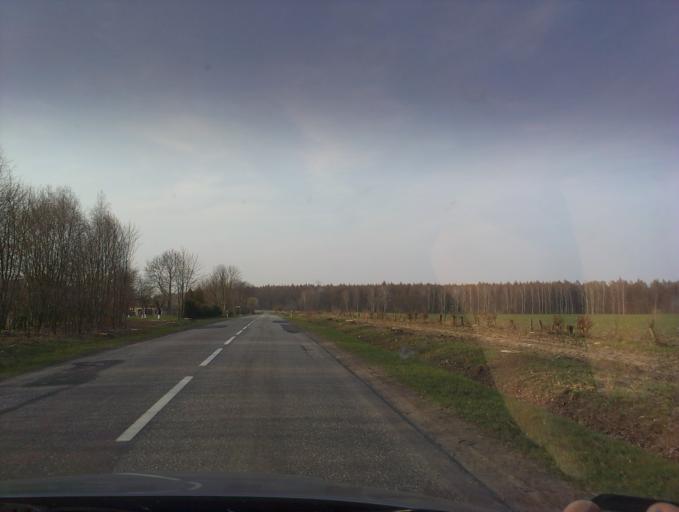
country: PL
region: Greater Poland Voivodeship
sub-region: Powiat zlotowski
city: Lipka
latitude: 53.5083
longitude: 17.2429
